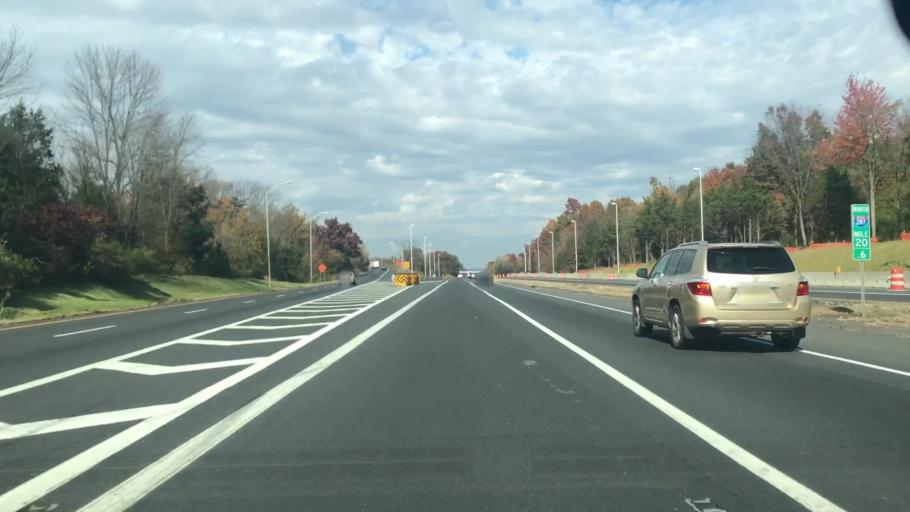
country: US
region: New Jersey
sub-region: Somerset County
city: Bridgewater
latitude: 40.6346
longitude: -74.6436
